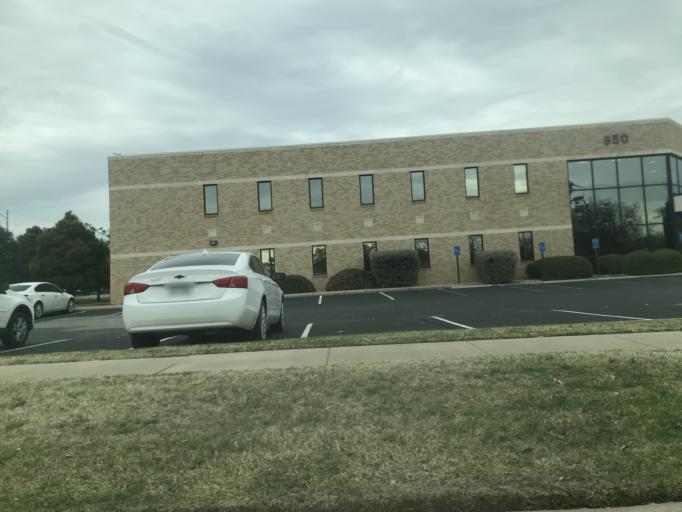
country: US
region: Texas
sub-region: Taylor County
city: Abilene
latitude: 32.4718
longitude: -99.7308
